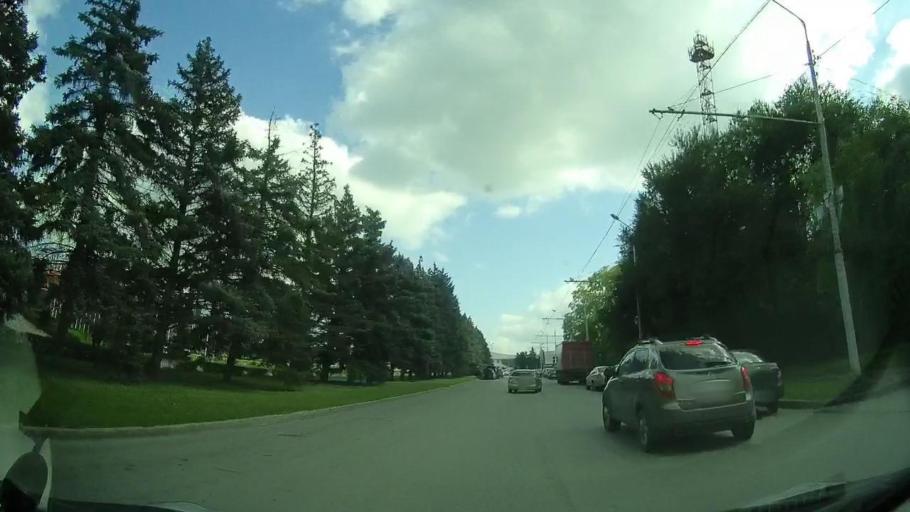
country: RU
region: Rostov
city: Imeni Chkalova
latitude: 47.2565
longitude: 39.8009
